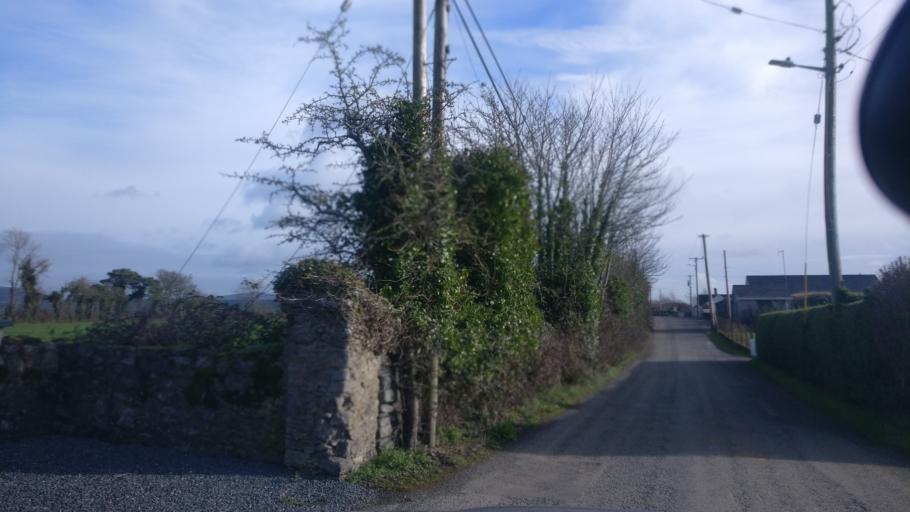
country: IE
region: Leinster
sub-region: Kilkenny
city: Thomastown
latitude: 52.5270
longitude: -7.1649
